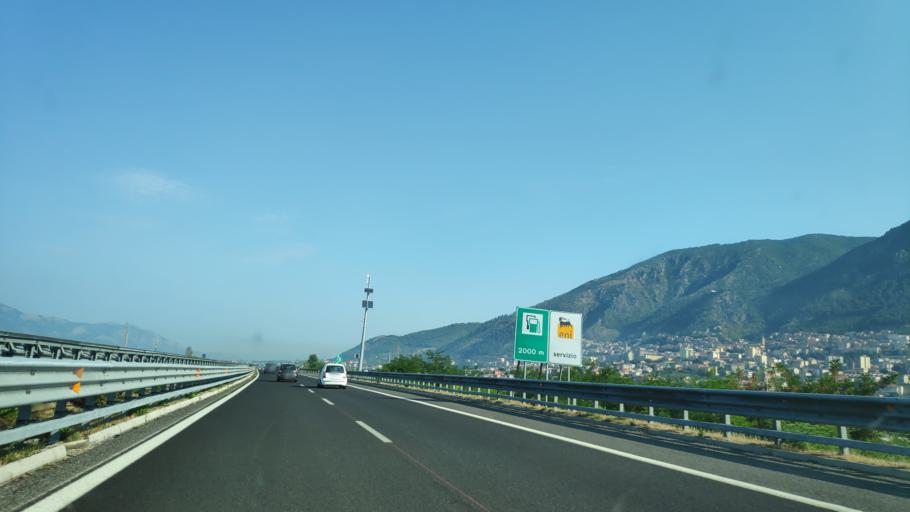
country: IT
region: Campania
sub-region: Provincia di Salerno
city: Sala Consilina
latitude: 40.3820
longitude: 15.5936
